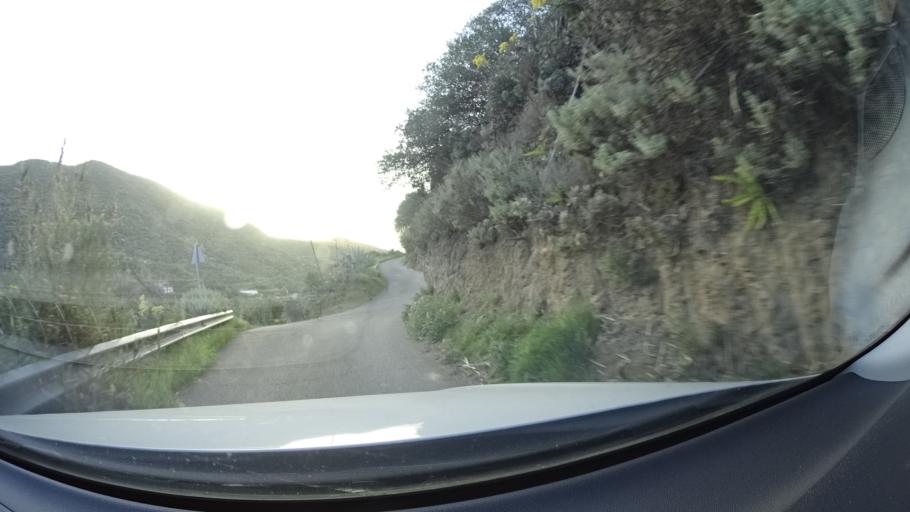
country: ES
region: Canary Islands
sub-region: Provincia de Las Palmas
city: Artenara
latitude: 28.0353
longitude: -15.6448
